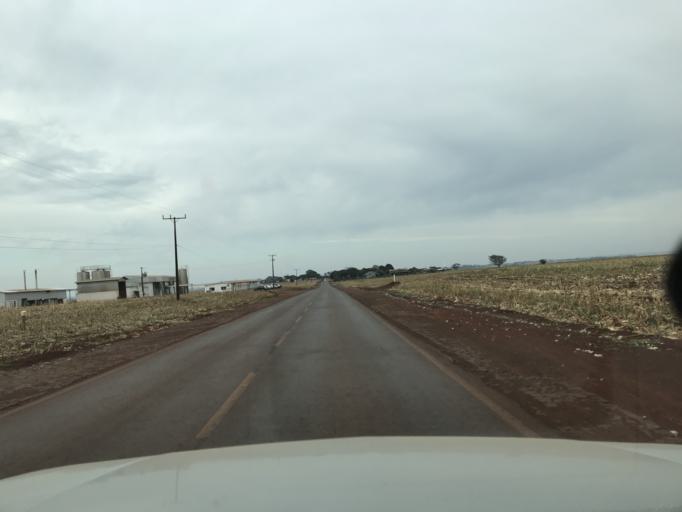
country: BR
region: Parana
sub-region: Palotina
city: Palotina
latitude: -24.4188
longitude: -53.8713
